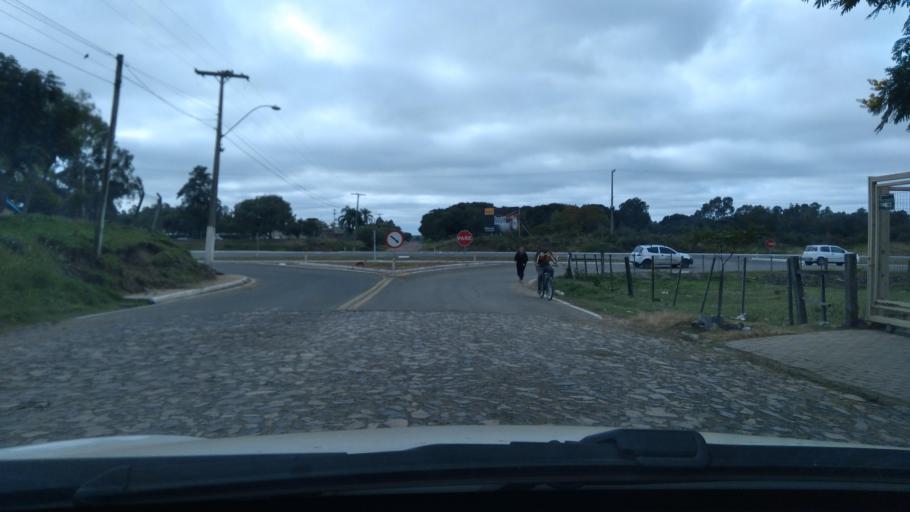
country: BR
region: Rio Grande do Sul
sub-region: Dom Pedrito
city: Dom Pedrito
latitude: -30.9640
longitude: -54.6719
